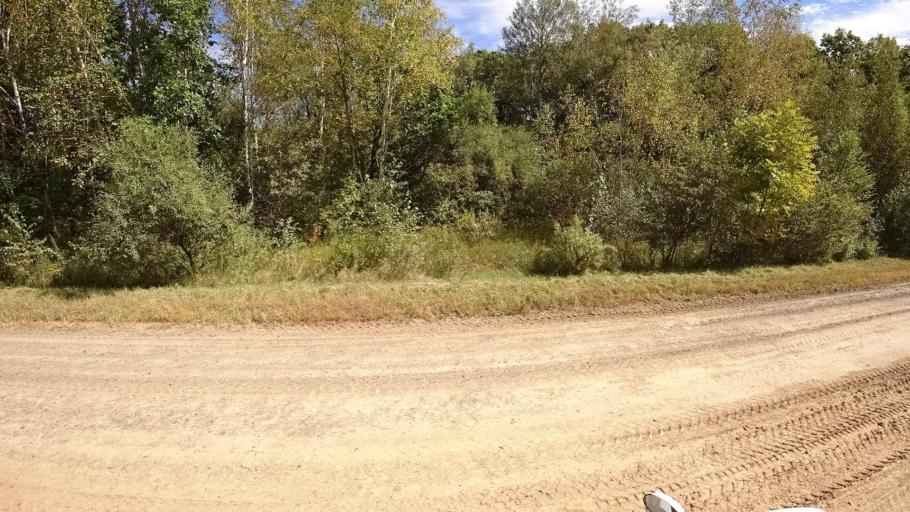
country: RU
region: Primorskiy
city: Yakovlevka
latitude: 44.7040
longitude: 133.6419
